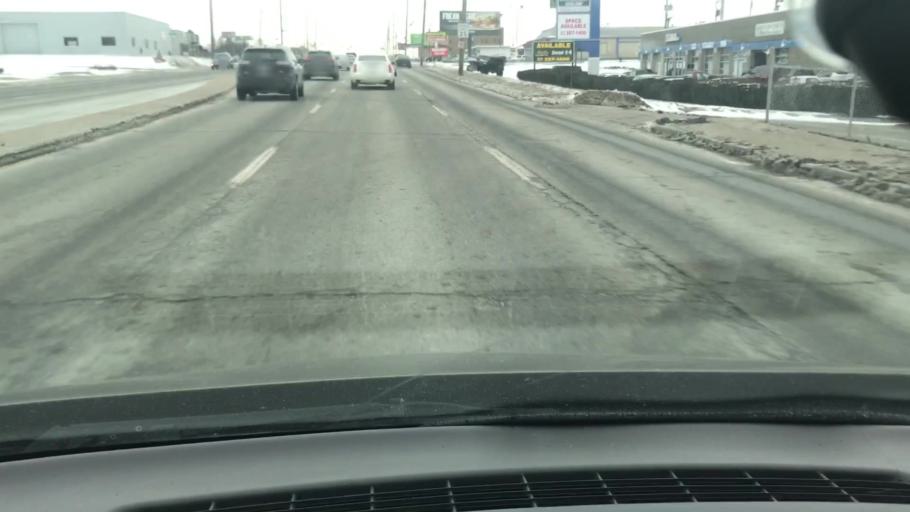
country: US
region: Indiana
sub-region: Marion County
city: Broad Ripple
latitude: 39.8376
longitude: -86.1218
